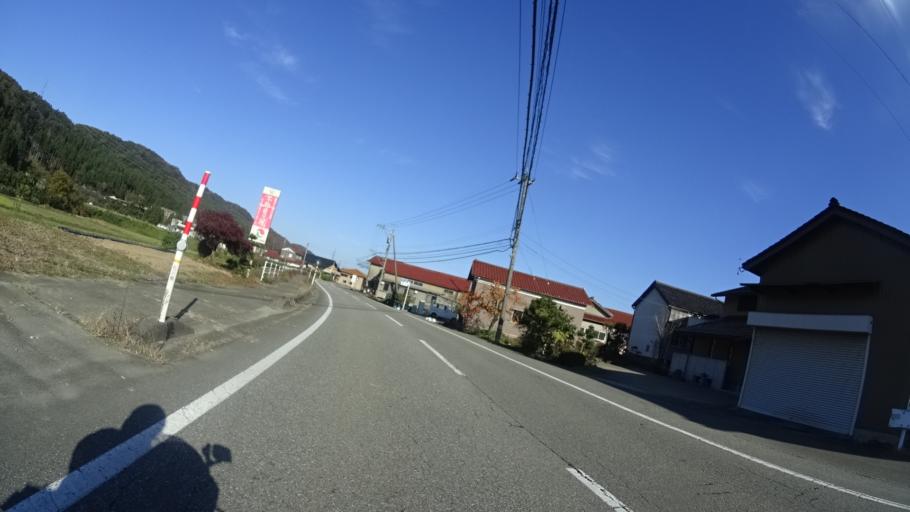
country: JP
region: Ishikawa
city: Komatsu
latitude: 36.2751
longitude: 136.3934
